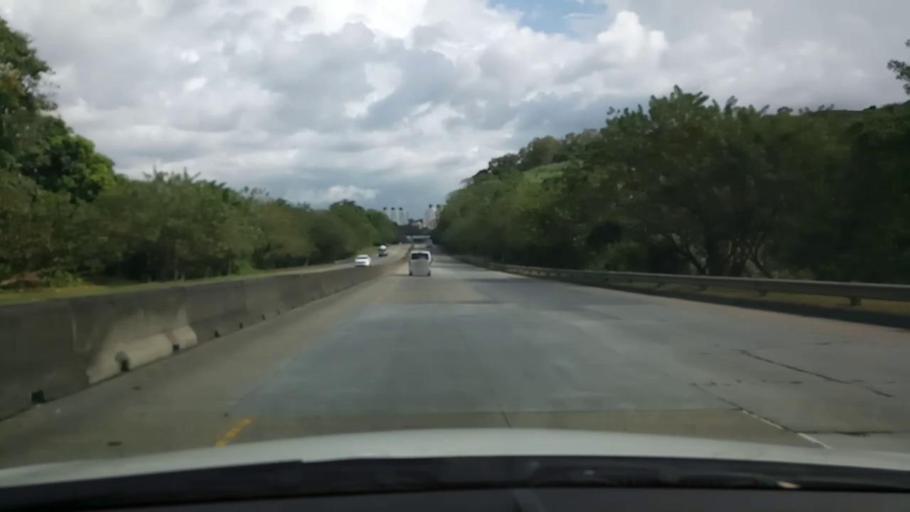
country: PA
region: Panama
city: Las Cumbres
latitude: 9.0441
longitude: -79.5397
